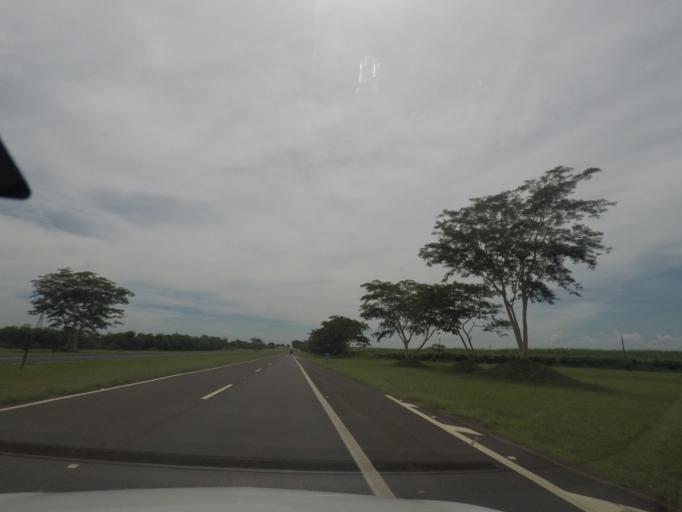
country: BR
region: Sao Paulo
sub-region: Bebedouro
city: Bebedouro
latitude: -20.9600
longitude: -48.4435
